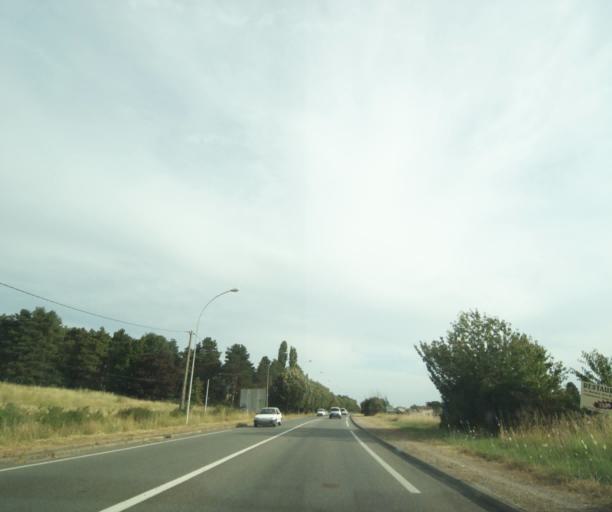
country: FR
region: Midi-Pyrenees
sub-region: Departement du Tarn-et-Garonne
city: Grisolles
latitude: 43.8335
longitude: 1.3013
